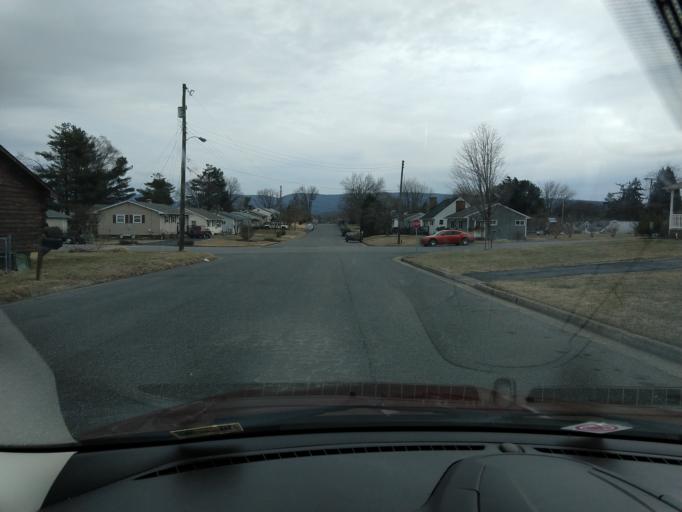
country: US
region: Virginia
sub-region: City of Waynesboro
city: Waynesboro
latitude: 38.0787
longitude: -78.9033
